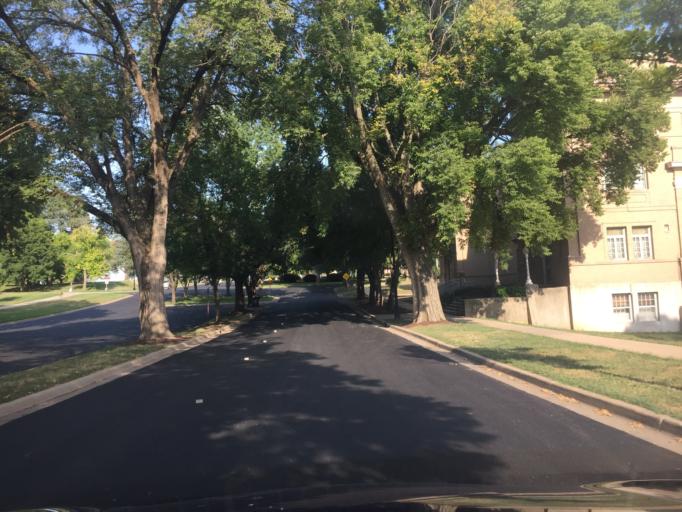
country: US
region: Kansas
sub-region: Leavenworth County
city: Leavenworth
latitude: 39.3554
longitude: -94.9190
